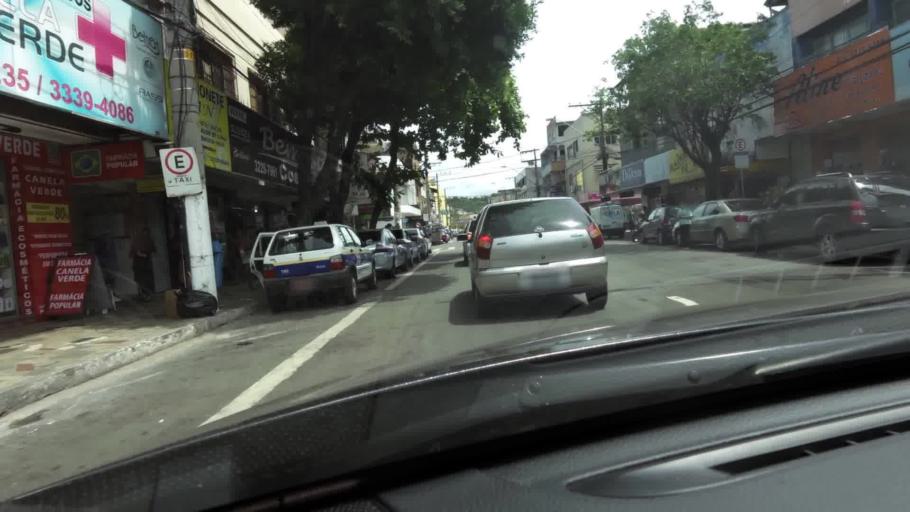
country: BR
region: Espirito Santo
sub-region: Vila Velha
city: Vila Velha
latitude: -20.3385
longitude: -40.3070
